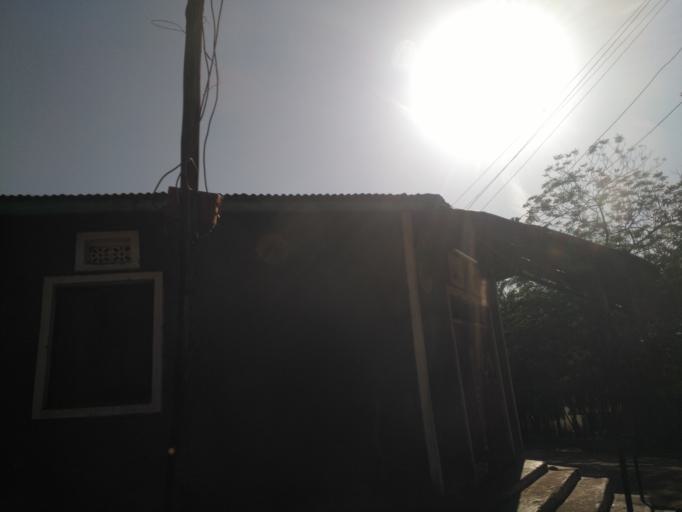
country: TZ
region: Mwanza
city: Mwanza
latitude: -2.5026
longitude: 32.8928
